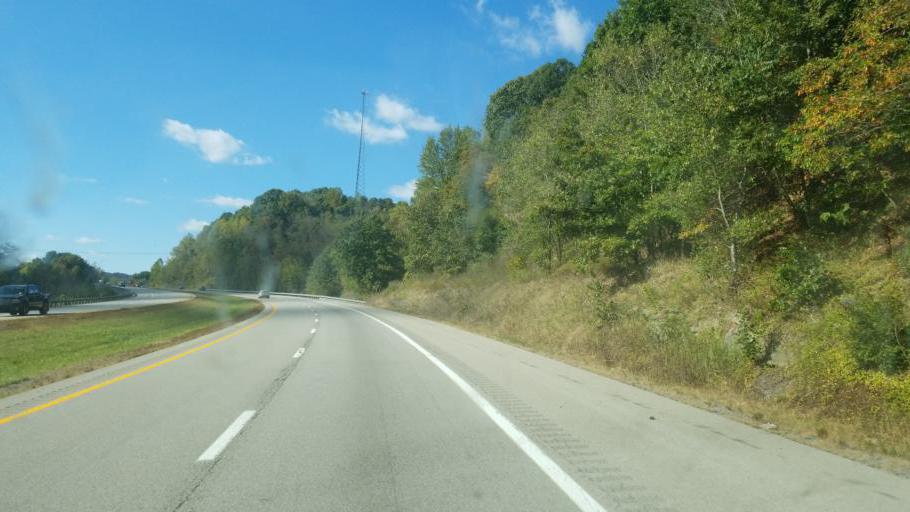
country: US
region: West Virginia
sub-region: Monongalia County
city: Star City
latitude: 39.6724
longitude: -80.0297
